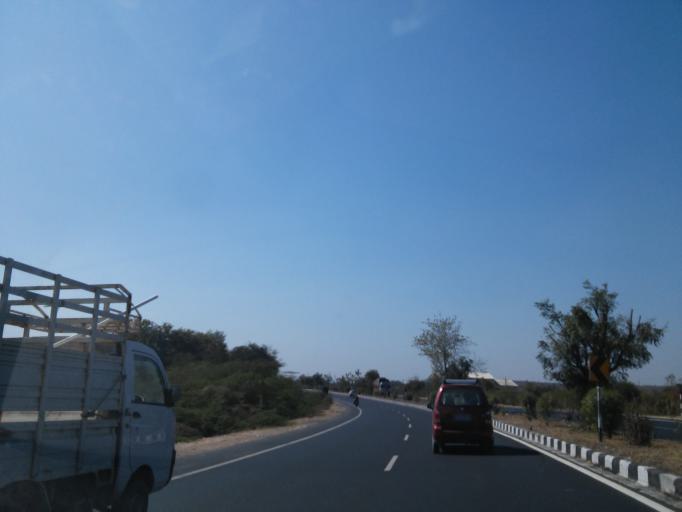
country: IN
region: Gujarat
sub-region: Sabar Kantha
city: Himatnagar
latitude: 23.5976
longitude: 73.0633
